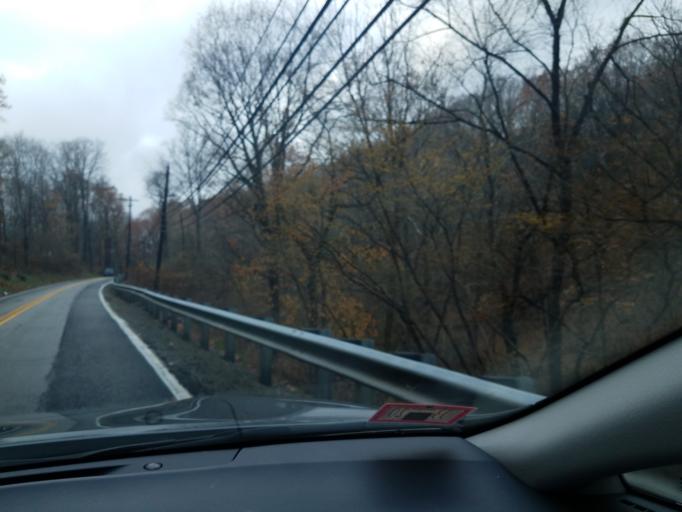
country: US
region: Pennsylvania
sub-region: Allegheny County
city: Franklin Park
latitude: 40.5657
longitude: -80.0638
